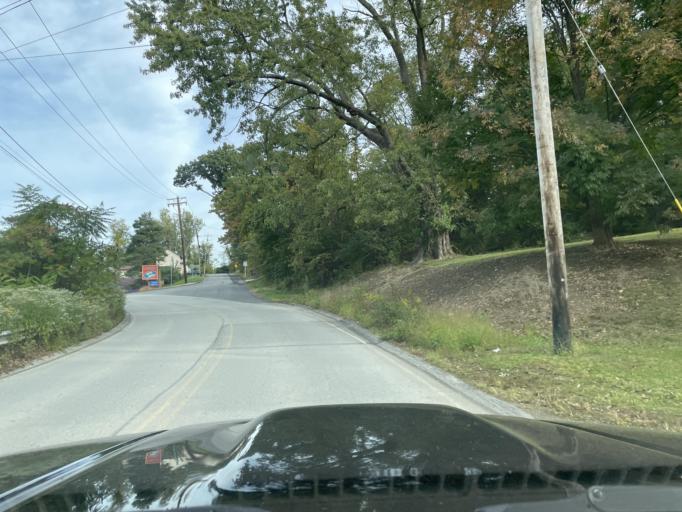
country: US
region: Pennsylvania
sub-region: Allegheny County
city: Monroeville
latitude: 40.4418
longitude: -79.7665
